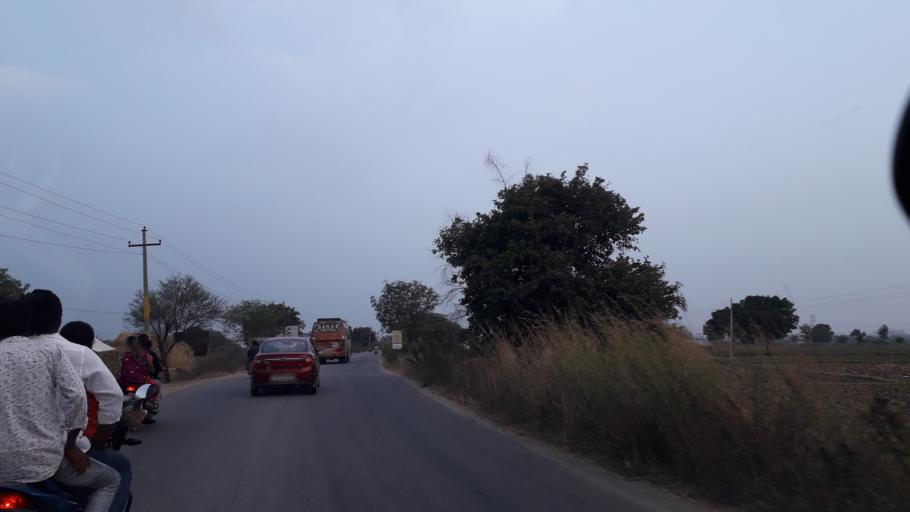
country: IN
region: Telangana
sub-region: Medak
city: Patancheru
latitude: 17.5130
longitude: 78.2248
